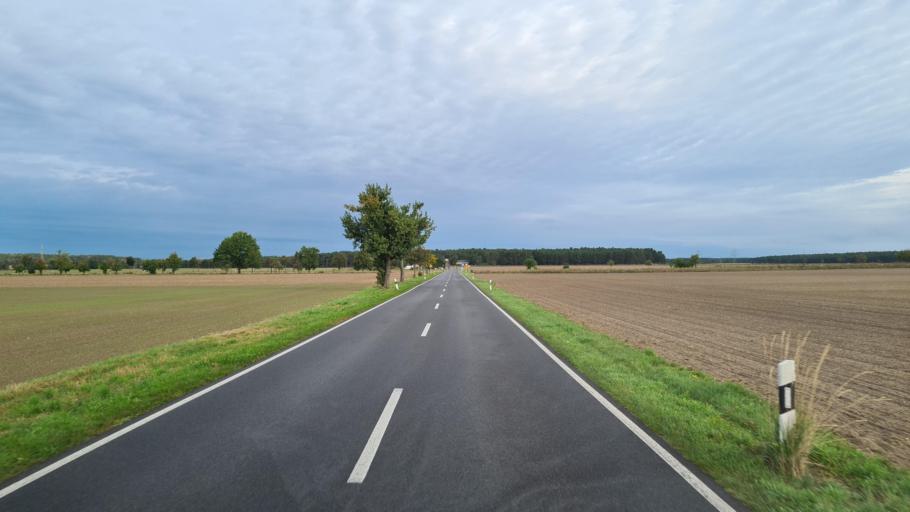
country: DE
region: Brandenburg
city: Luckau
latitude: 51.8799
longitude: 13.7203
